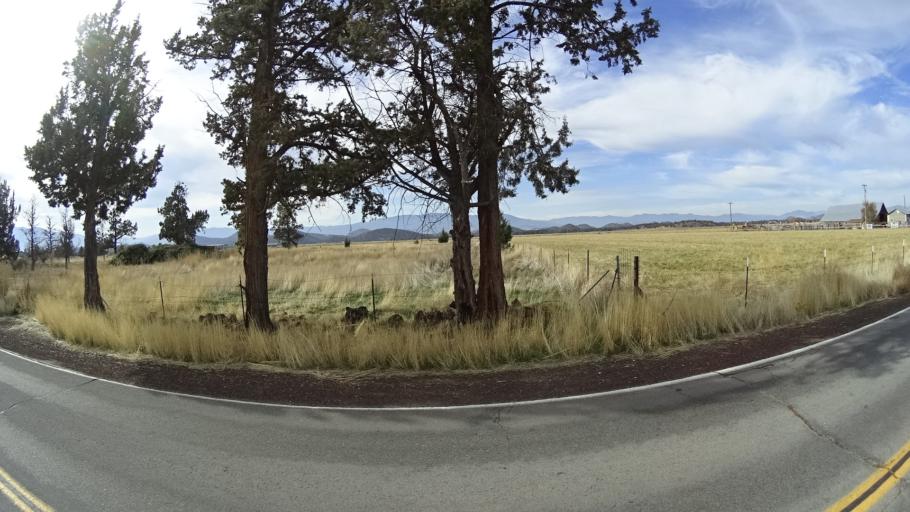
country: US
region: California
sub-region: Siskiyou County
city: Montague
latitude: 41.6133
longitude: -122.3996
